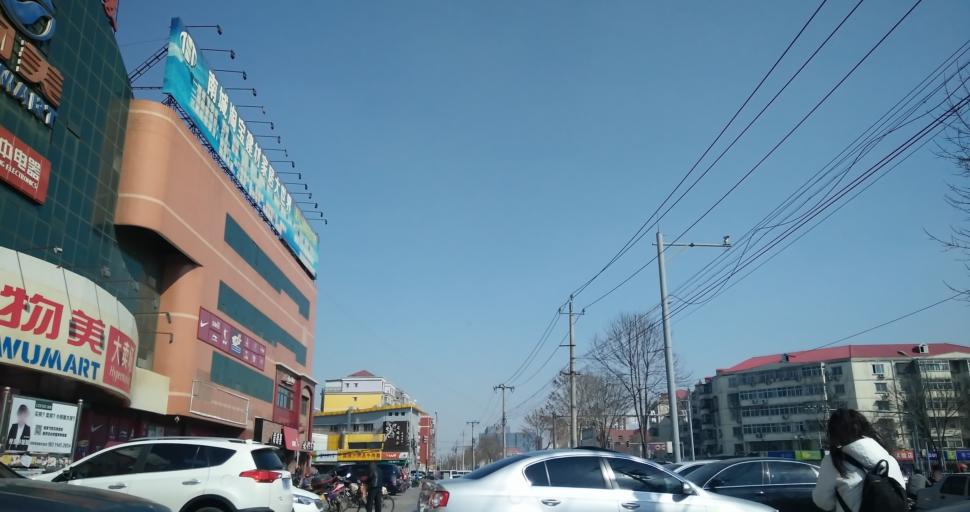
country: CN
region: Beijing
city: Jiugong
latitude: 39.8037
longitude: 116.4367
